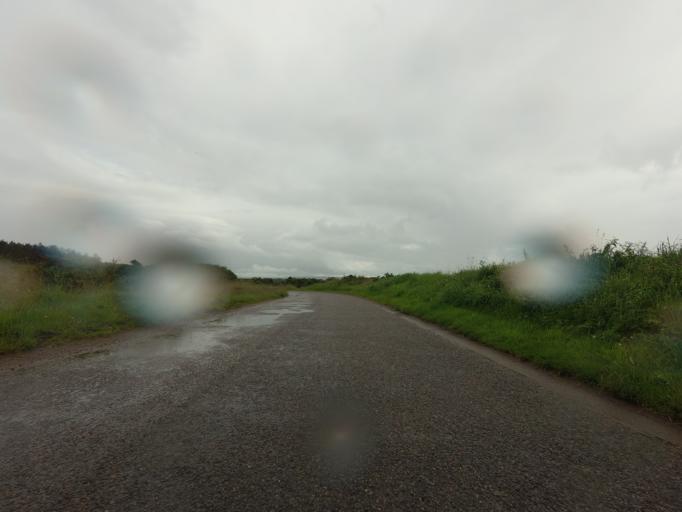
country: GB
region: Scotland
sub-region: Moray
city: Fochabers
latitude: 57.6590
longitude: -3.0729
